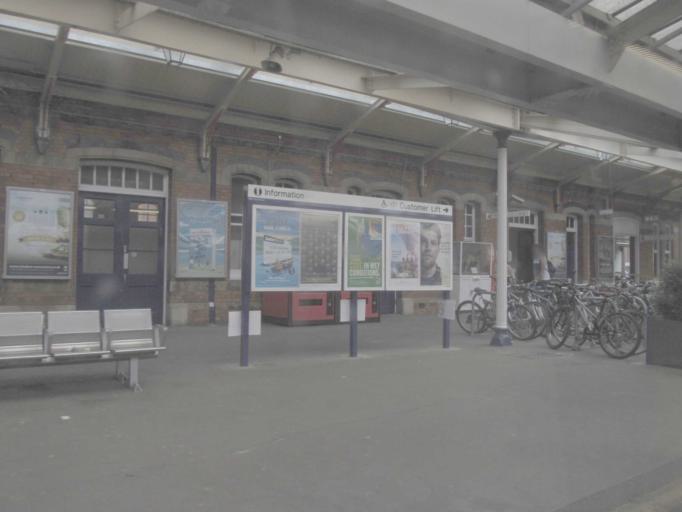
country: GB
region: England
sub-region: Slough
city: Slough
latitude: 51.5136
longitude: -0.5926
